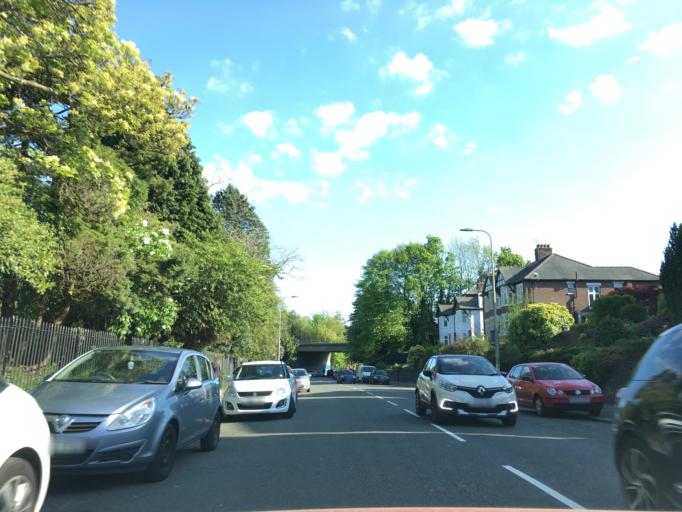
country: GB
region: Wales
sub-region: Cardiff
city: Cardiff
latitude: 51.5043
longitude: -3.1763
